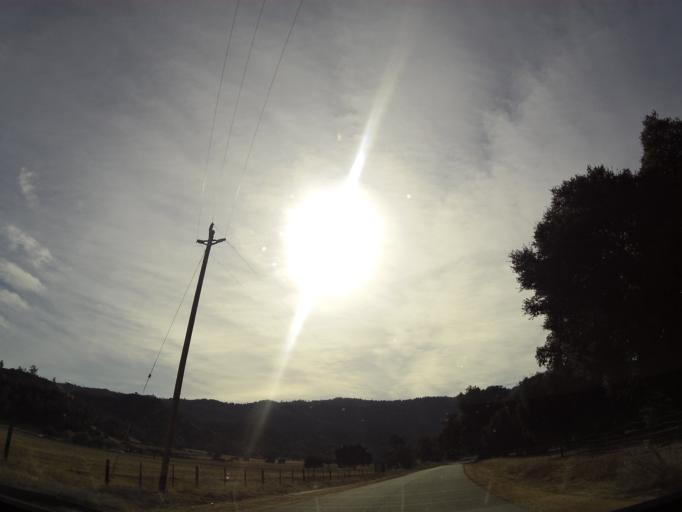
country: US
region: California
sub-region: San Benito County
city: Ridgemark
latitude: 36.6983
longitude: -121.3302
